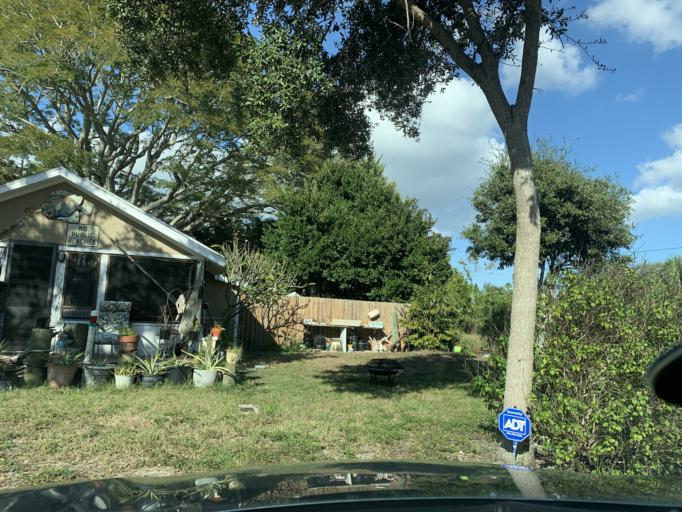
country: US
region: Florida
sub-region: Pinellas County
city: Belleair
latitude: 27.9342
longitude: -82.7940
